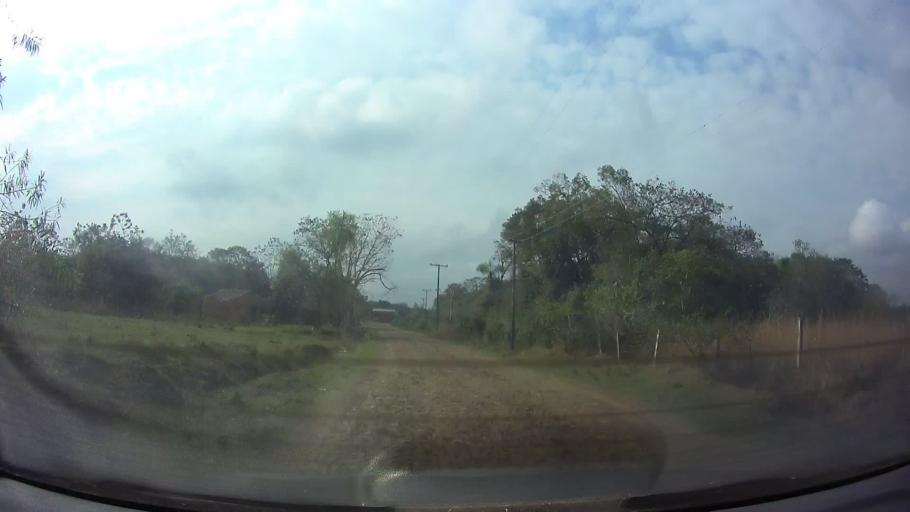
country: PY
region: Cordillera
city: Arroyos y Esteros
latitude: -24.9982
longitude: -57.1945
